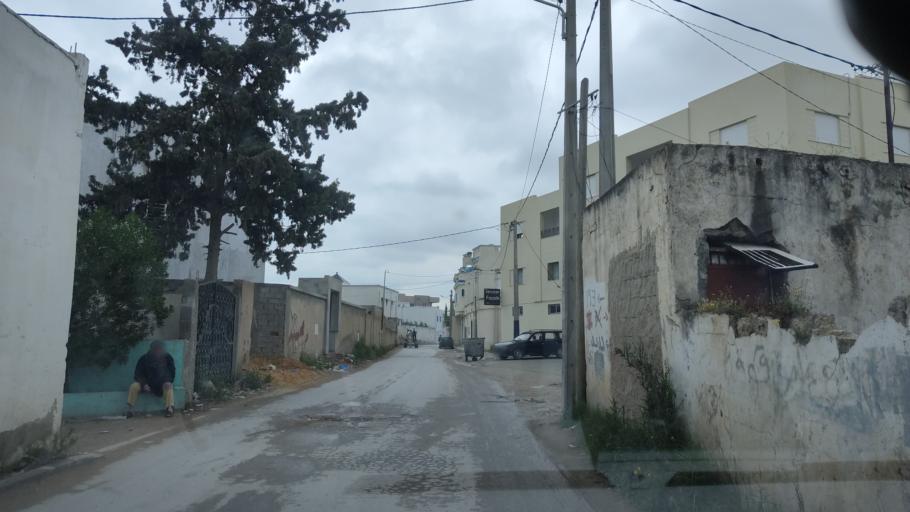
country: TN
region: Ariana
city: Ariana
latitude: 36.8834
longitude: 10.2187
